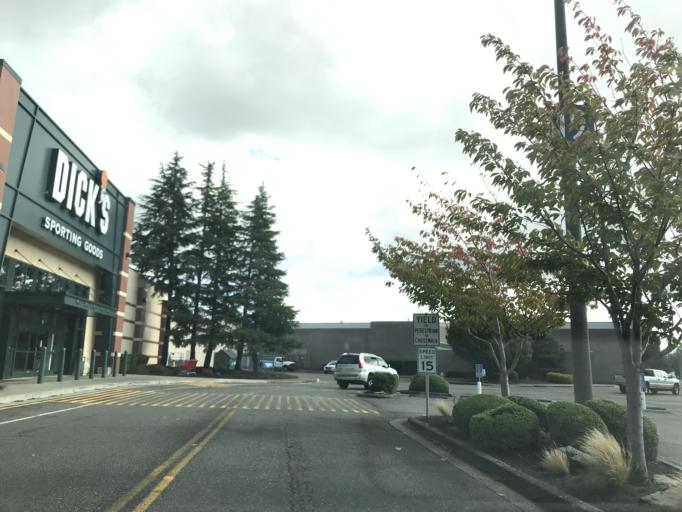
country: US
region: Washington
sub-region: Whatcom County
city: Bellingham
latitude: 48.7848
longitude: -122.4931
